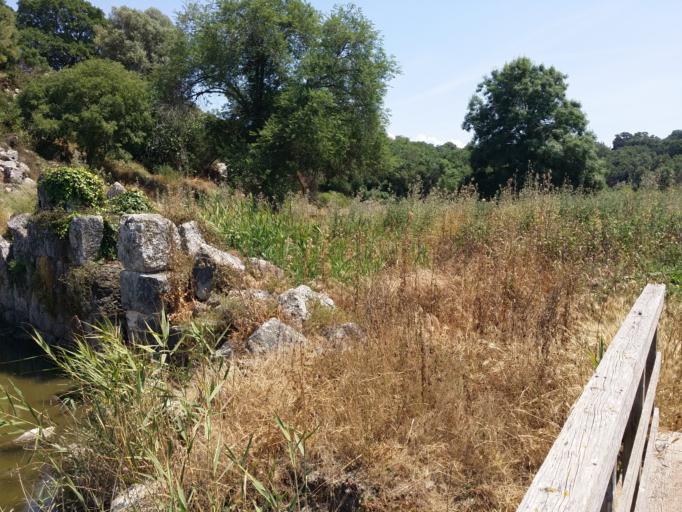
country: GR
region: West Greece
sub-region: Nomos Aitolias kai Akarnanias
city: Neochorion
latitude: 38.4113
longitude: 21.1934
